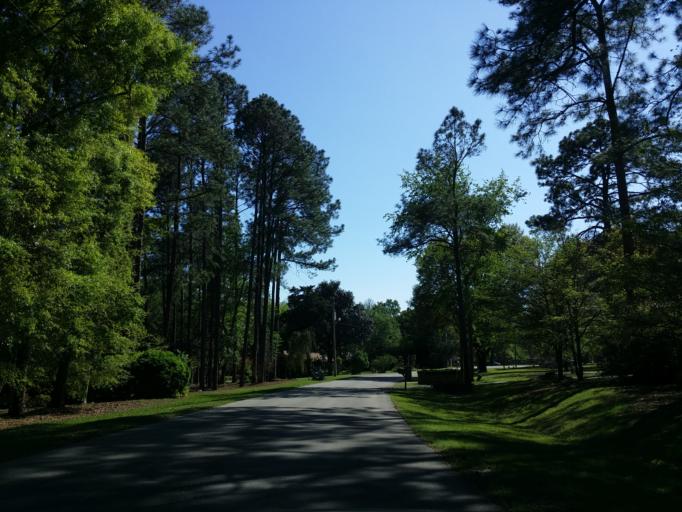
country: US
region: Florida
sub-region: Leon County
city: Tallahassee
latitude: 30.4795
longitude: -84.1810
